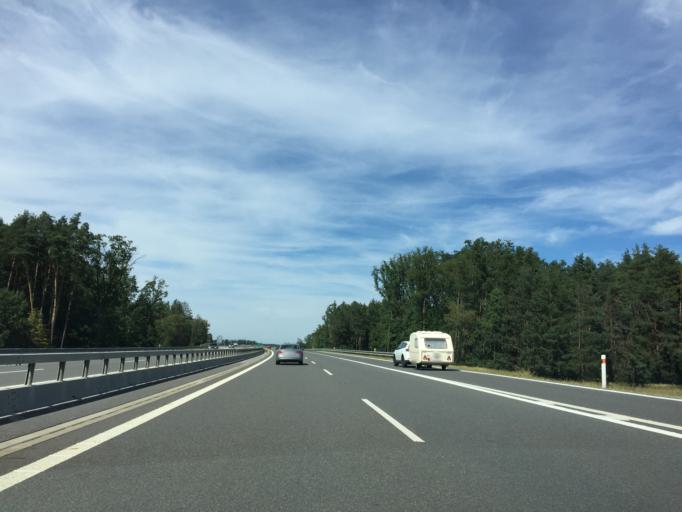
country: CZ
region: Jihocesky
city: Sobeslav
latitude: 49.2254
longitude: 14.7281
